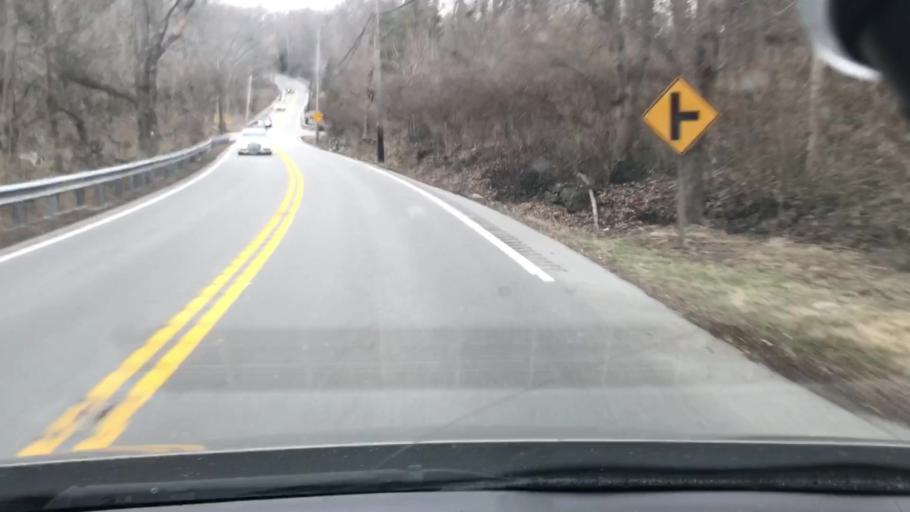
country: US
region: Kentucky
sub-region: Jefferson County
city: Barbourmeade
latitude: 38.2925
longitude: -85.6088
